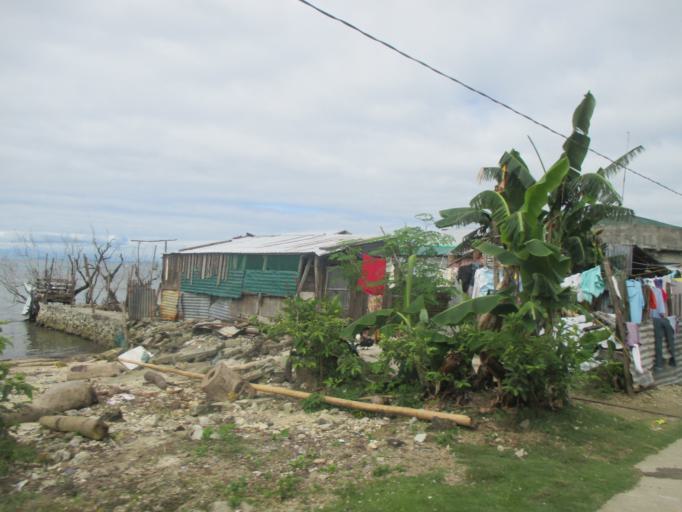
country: PH
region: Eastern Visayas
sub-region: Province of Eastern Samar
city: Lawa-an
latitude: 11.1090
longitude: 125.2120
